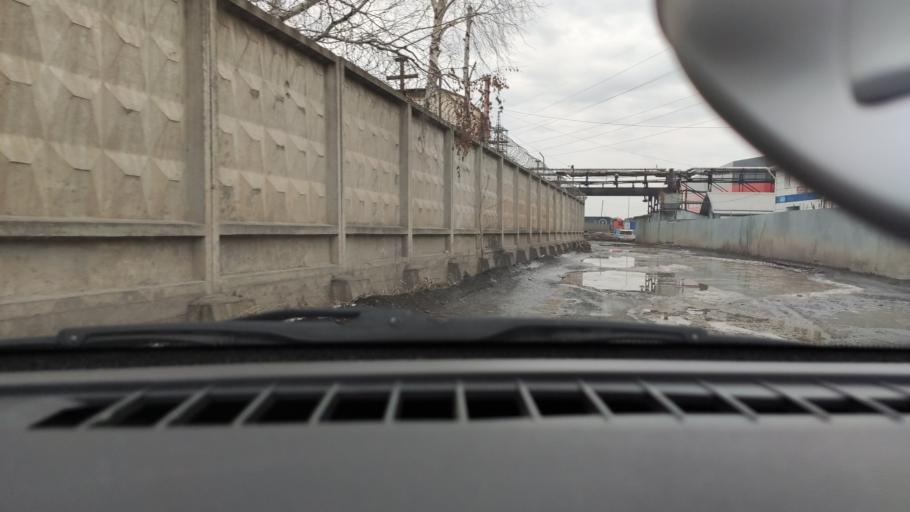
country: RU
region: Perm
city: Perm
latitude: 58.0422
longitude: 56.3110
